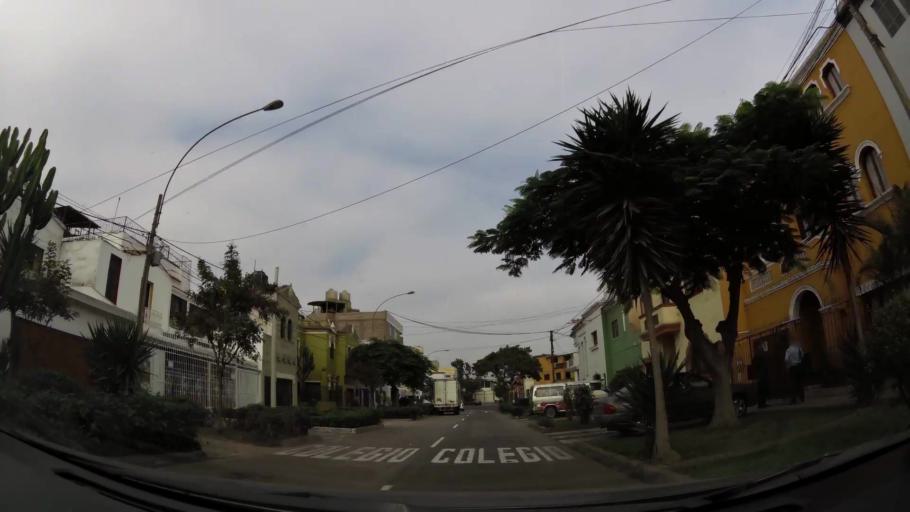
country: PE
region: Lima
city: Lima
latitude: -12.0767
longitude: -77.0475
